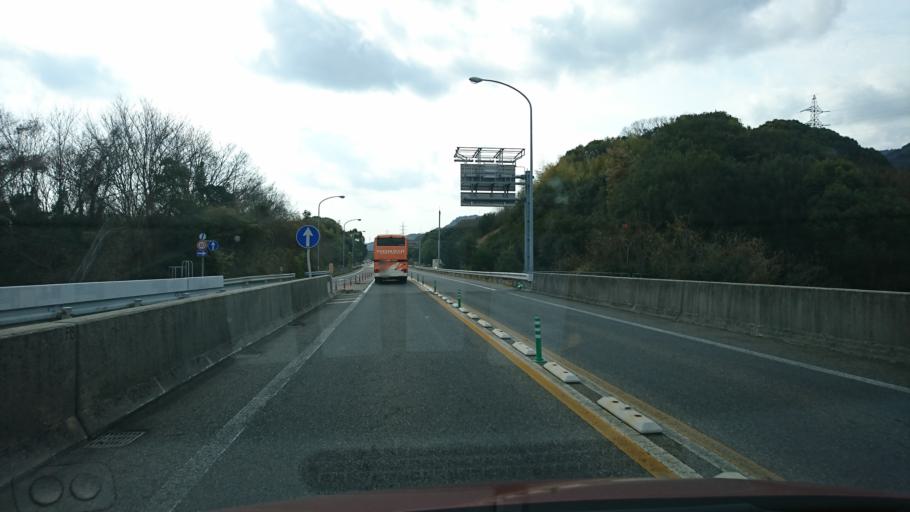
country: JP
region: Hiroshima
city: Innoshima
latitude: 34.2477
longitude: 133.0484
